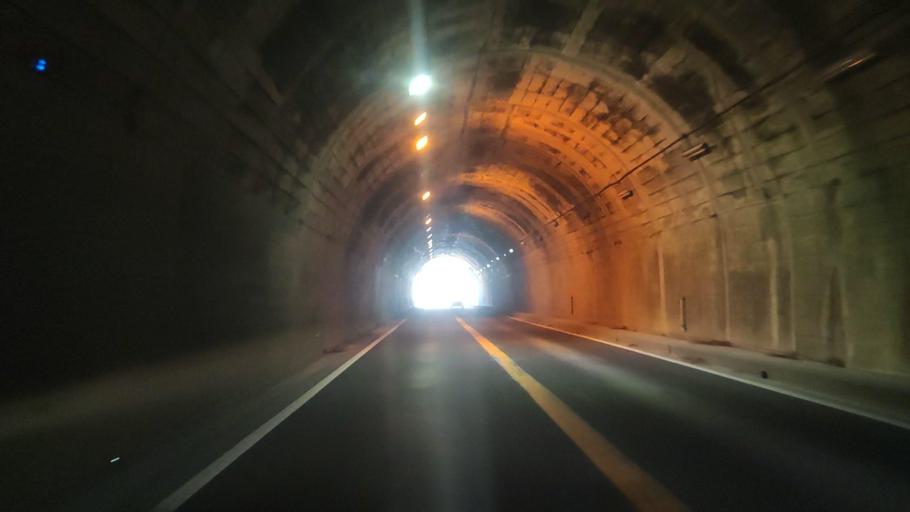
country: JP
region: Oita
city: Saiki
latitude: 32.9916
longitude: 131.8300
